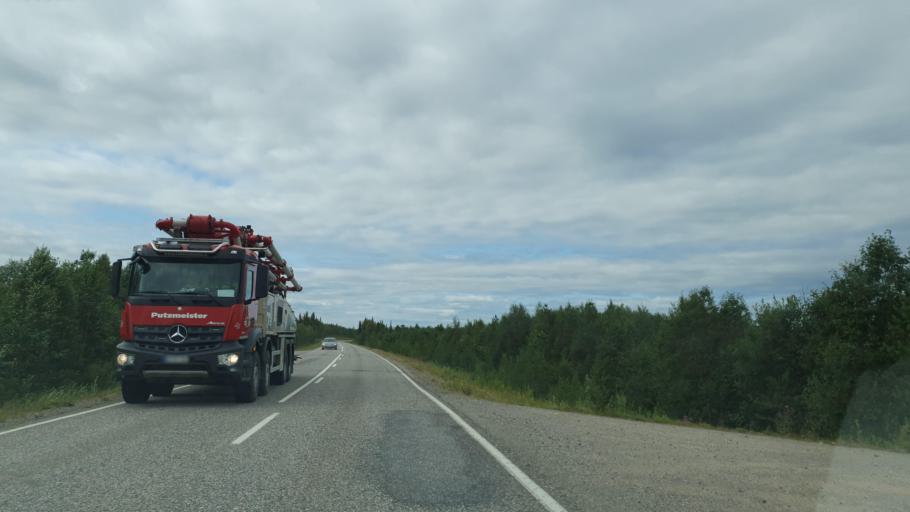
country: FI
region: Lapland
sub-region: Tunturi-Lappi
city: Kittilae
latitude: 67.6620
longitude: 24.7999
